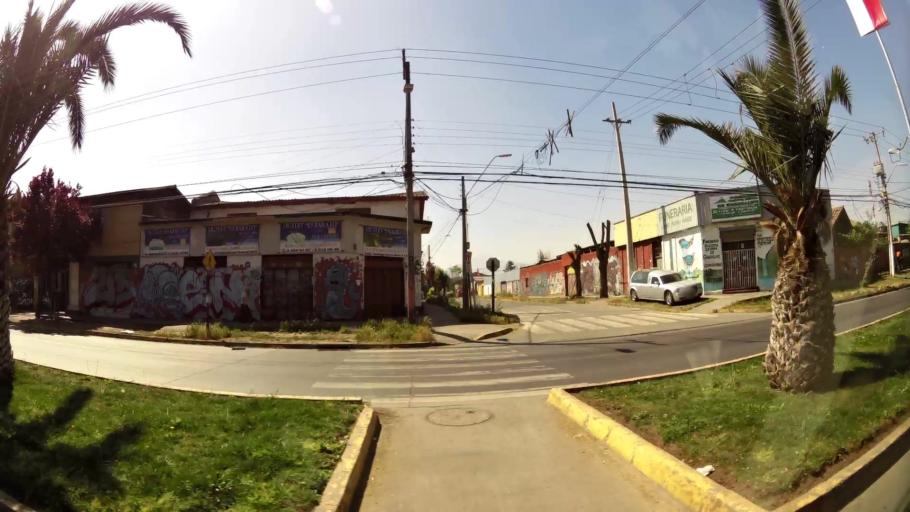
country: CL
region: Santiago Metropolitan
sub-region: Provincia de Santiago
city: Lo Prado
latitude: -33.4105
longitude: -70.6889
